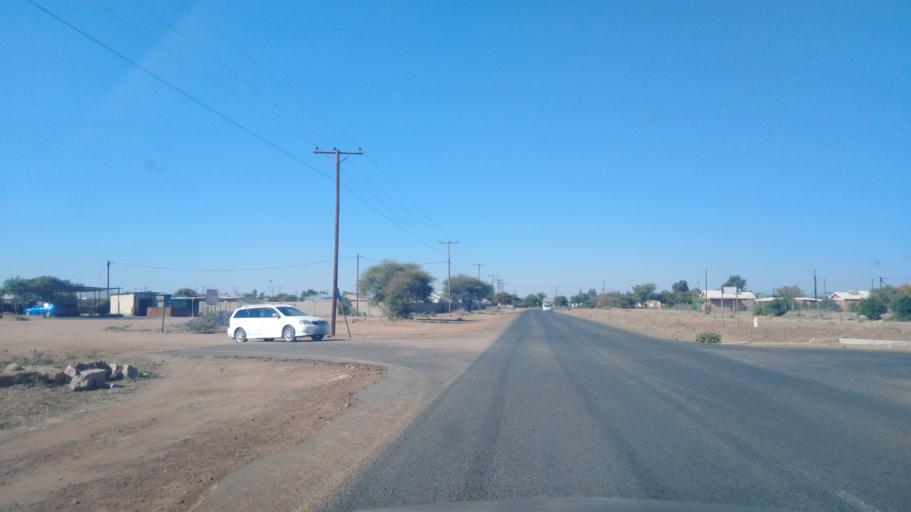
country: BW
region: Central
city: Mahalapye
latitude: -23.1220
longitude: 26.7952
